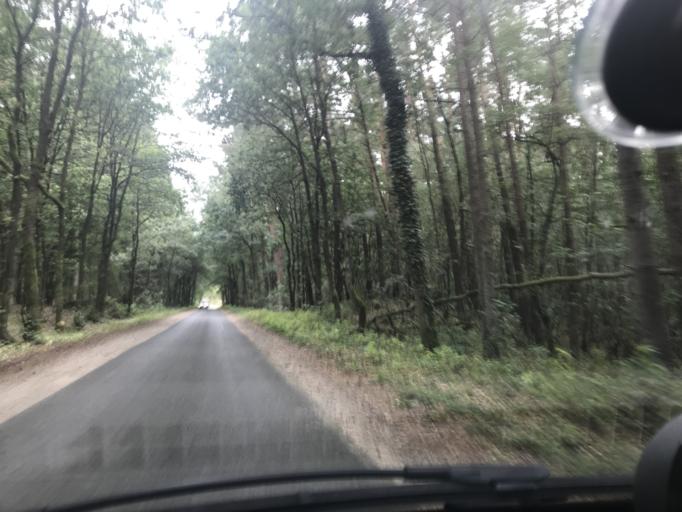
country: DE
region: Lower Saxony
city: Moisburg
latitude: 53.3926
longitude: 9.7249
